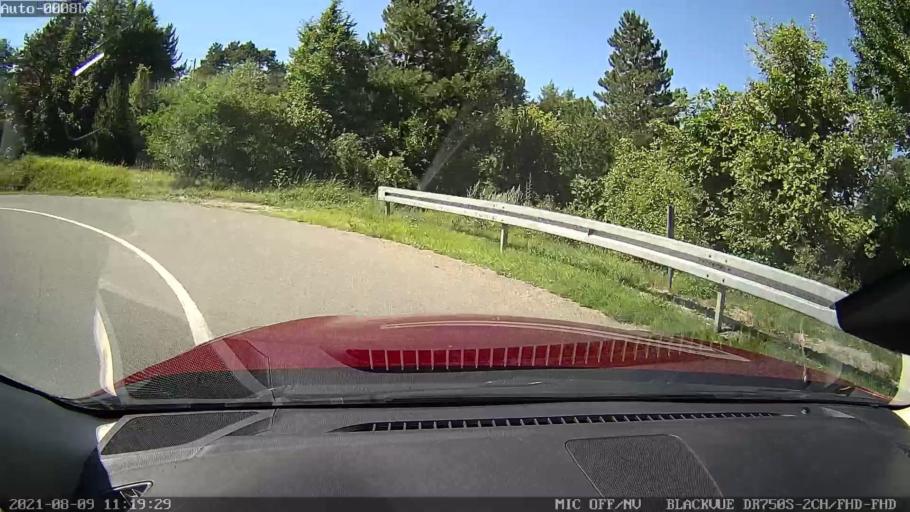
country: HR
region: Istarska
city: Lovran
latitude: 45.3058
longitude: 14.1941
